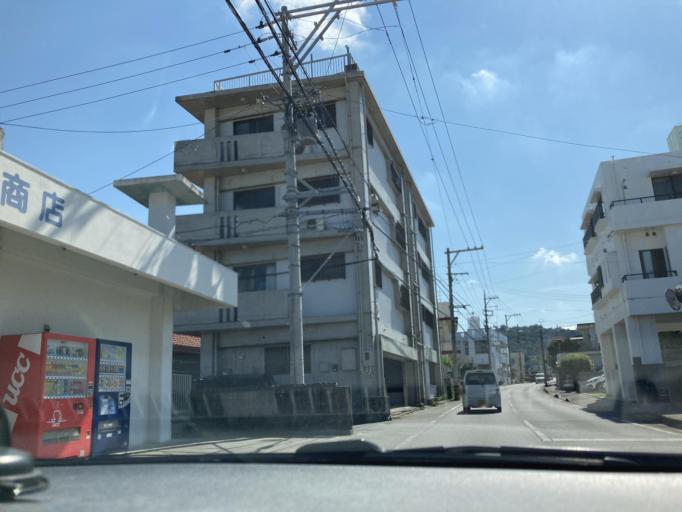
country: JP
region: Okinawa
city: Ginowan
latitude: 26.2243
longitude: 127.7543
